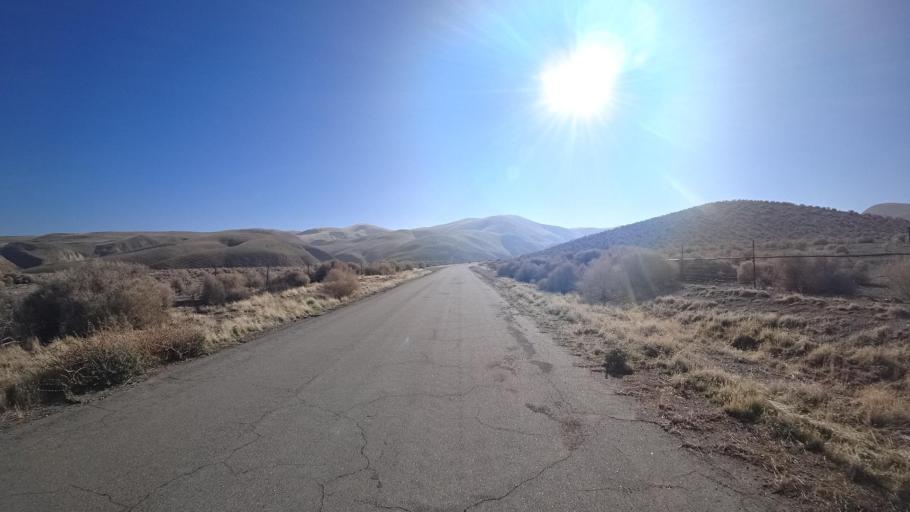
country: US
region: California
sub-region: Kern County
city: Maricopa
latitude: 34.9866
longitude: -119.3934
